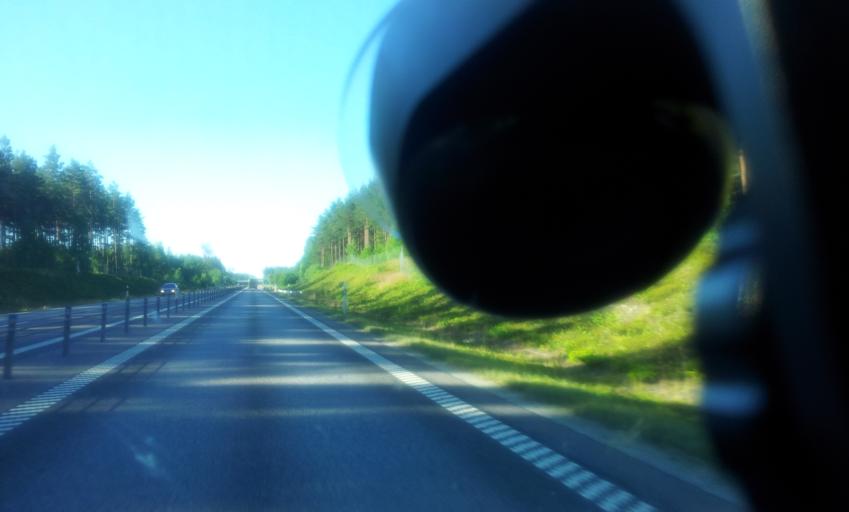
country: SE
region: Kalmar
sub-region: Kalmar Kommun
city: Ljungbyholm
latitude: 56.5221
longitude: 16.0852
